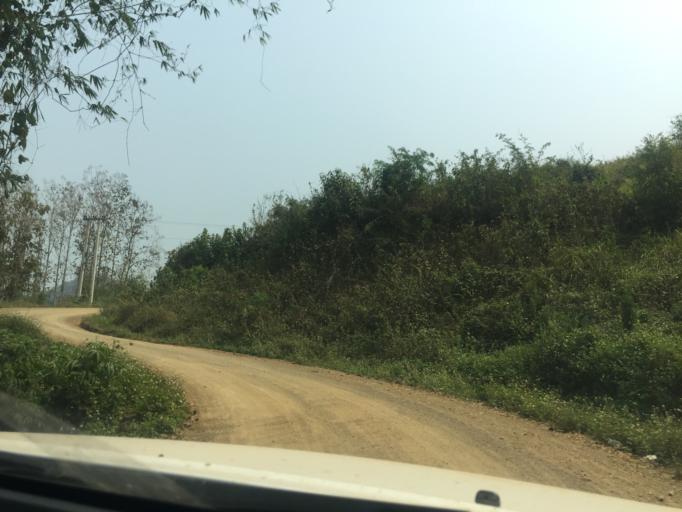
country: LA
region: Loungnamtha
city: Muang Nale
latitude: 20.3026
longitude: 101.6567
